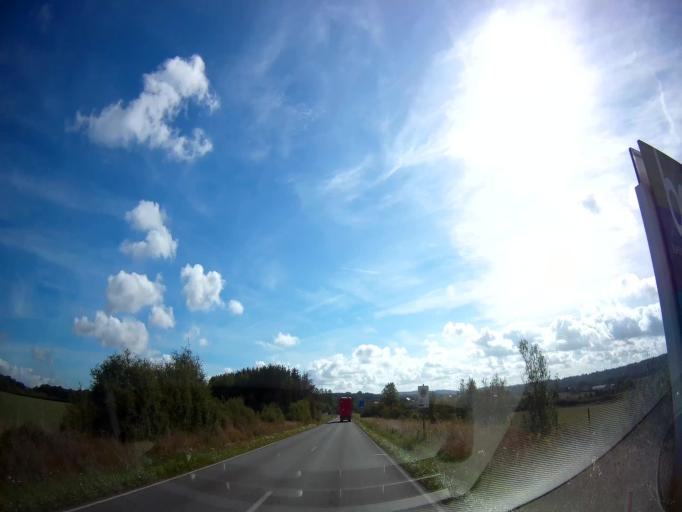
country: BE
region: Wallonia
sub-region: Province de Namur
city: Rochefort
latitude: 50.1673
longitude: 5.1904
